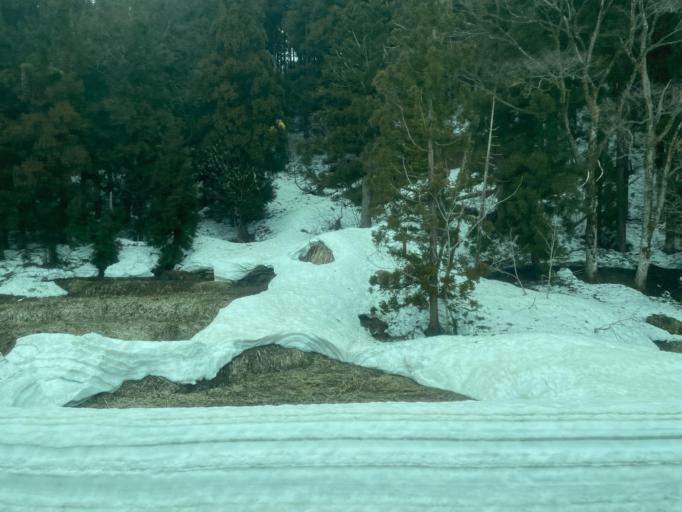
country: JP
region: Niigata
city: Shiozawa
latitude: 37.0166
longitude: 138.8176
